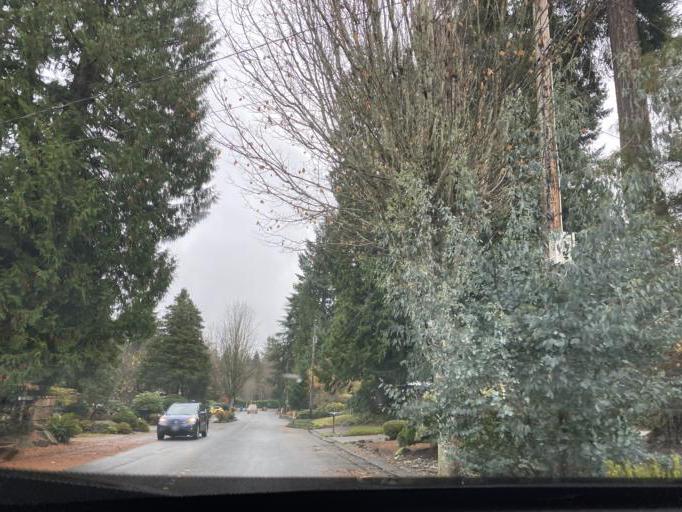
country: US
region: Washington
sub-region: King County
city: Mercer Island
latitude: 47.5461
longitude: -122.2242
